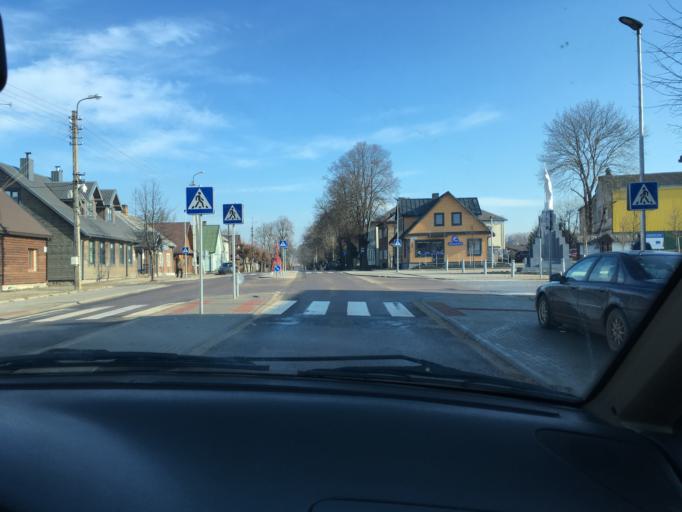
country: LT
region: Panevezys
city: Rokiskis
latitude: 55.7465
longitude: 25.8399
